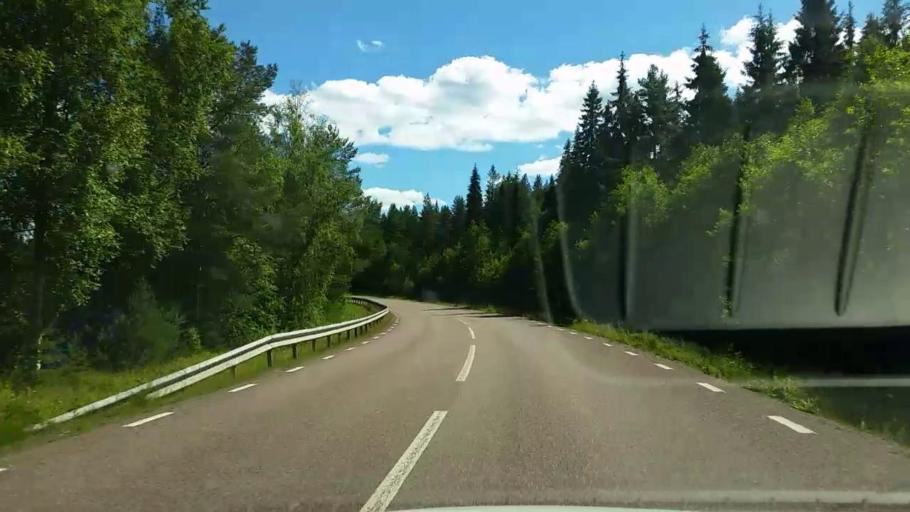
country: SE
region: Dalarna
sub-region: Faluns Kommun
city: Svardsjo
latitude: 60.9586
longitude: 15.6917
